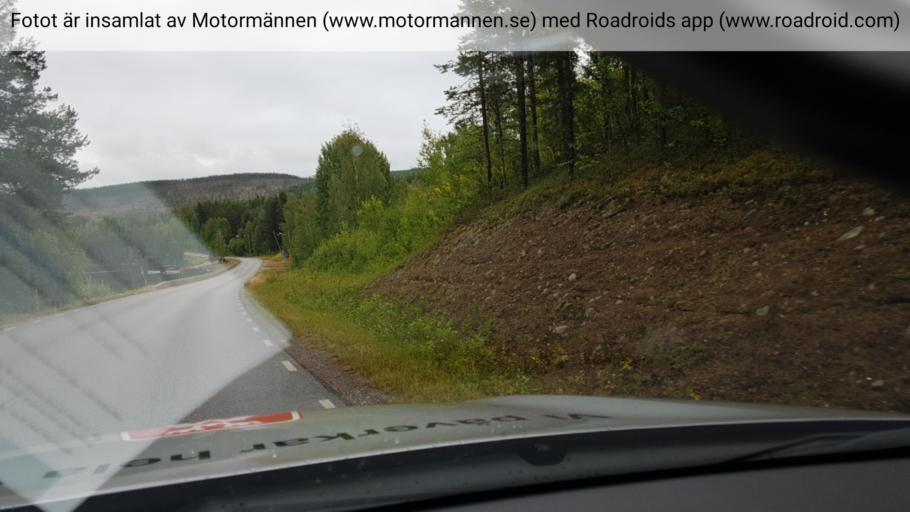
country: SE
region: Norrbotten
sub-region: Gallivare Kommun
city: Gaellivare
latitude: 66.4491
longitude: 20.6534
